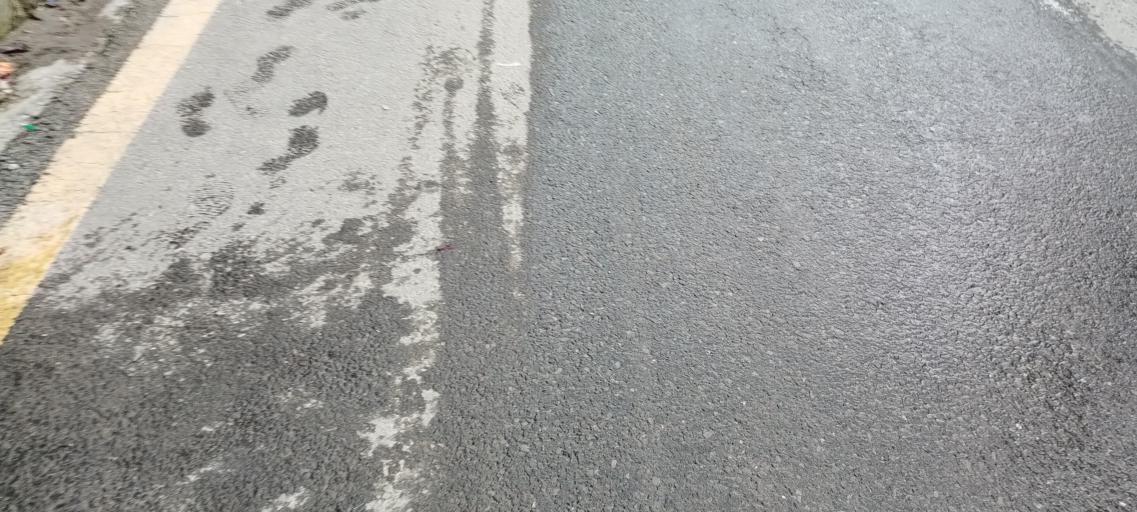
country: NP
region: Central Region
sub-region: Bagmati Zone
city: Kathmandu
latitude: 27.7803
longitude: 85.3636
